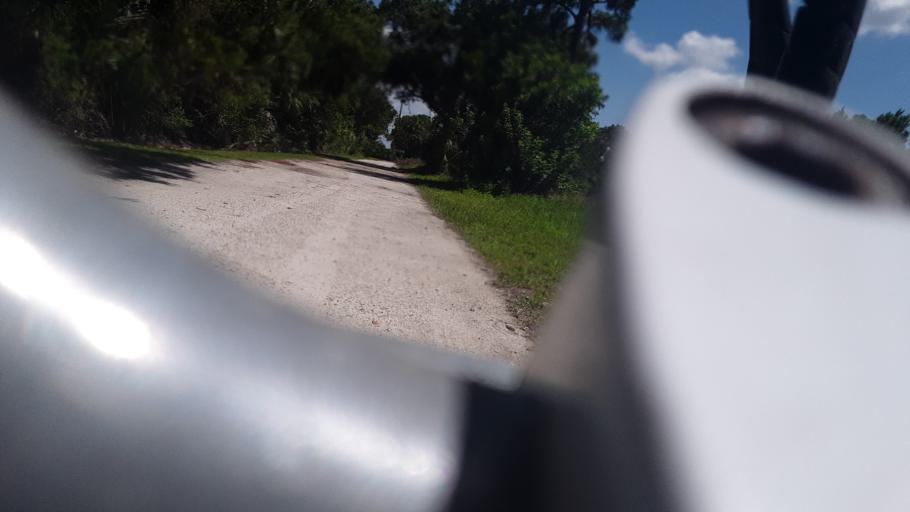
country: US
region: Florida
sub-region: Brevard County
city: Palm Bay
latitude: 27.9930
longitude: -80.6140
